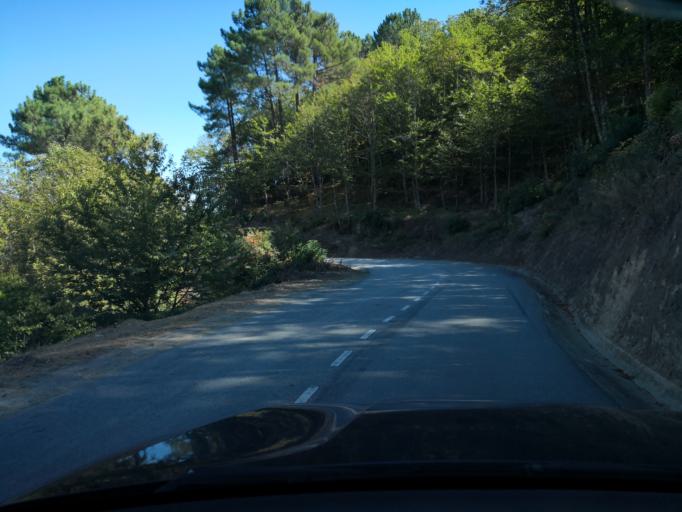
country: PT
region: Vila Real
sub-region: Santa Marta de Penaguiao
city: Santa Marta de Penaguiao
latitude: 41.2408
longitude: -7.8062
